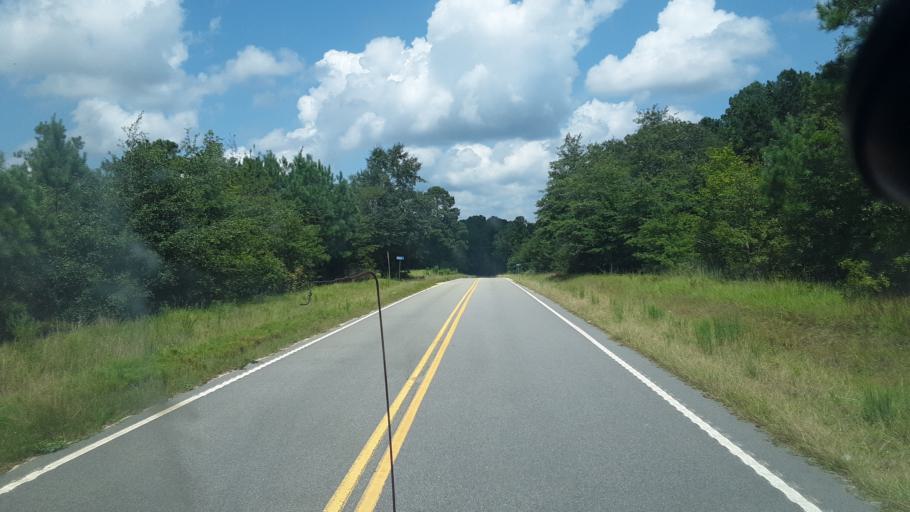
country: US
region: South Carolina
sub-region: Calhoun County
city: Oak Grove
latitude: 33.7039
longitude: -80.9541
